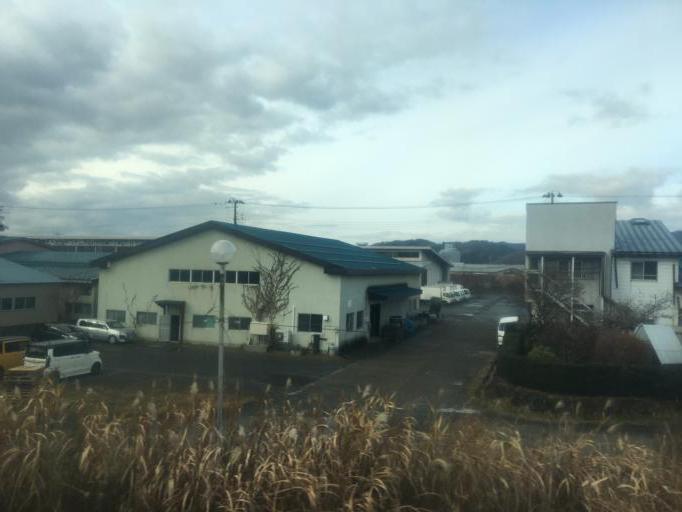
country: JP
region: Akita
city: Odate
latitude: 40.2944
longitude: 140.5662
